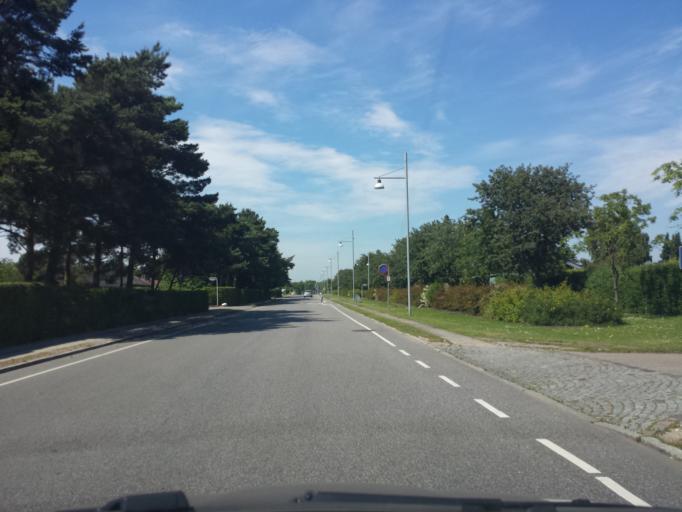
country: DK
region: Capital Region
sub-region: Glostrup Kommune
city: Glostrup
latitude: 55.6997
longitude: 12.4043
